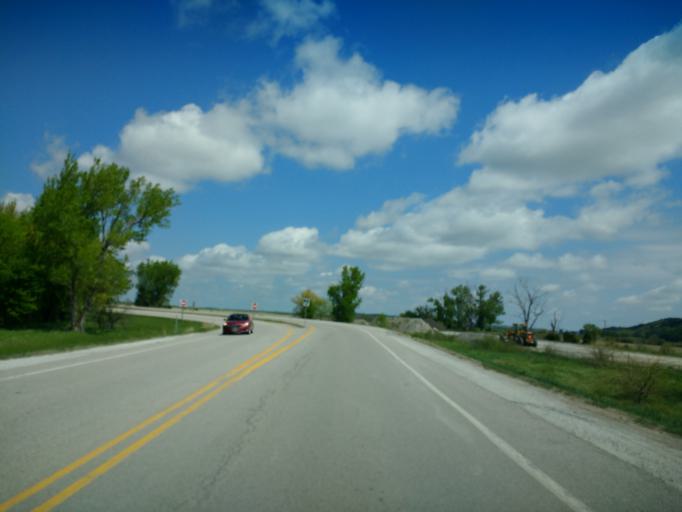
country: US
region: Iowa
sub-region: Harrison County
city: Missouri Valley
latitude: 41.5001
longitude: -95.8992
